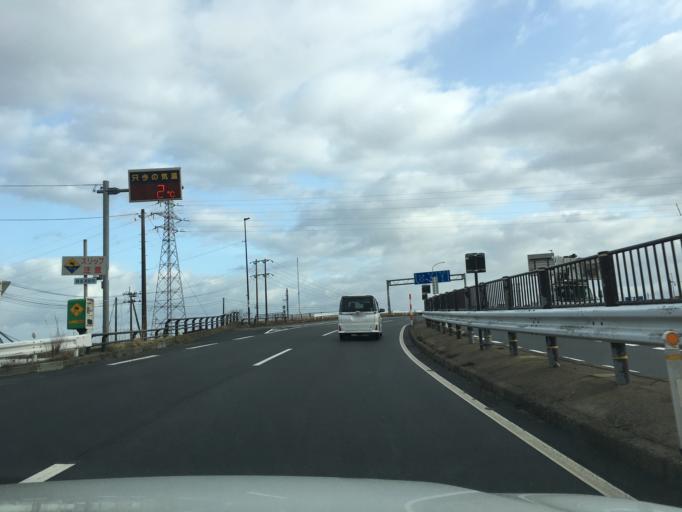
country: JP
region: Yamagata
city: Sakata
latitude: 38.8825
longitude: 139.8379
